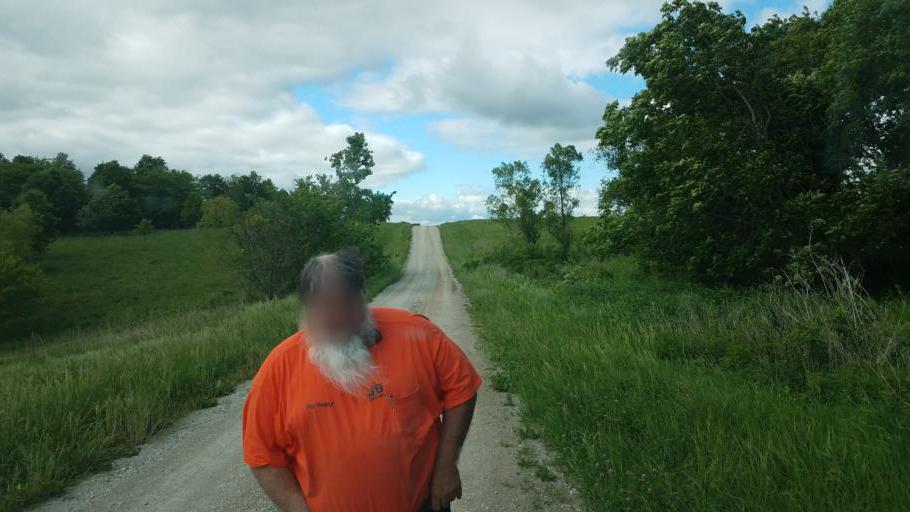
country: US
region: Missouri
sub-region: Grundy County
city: Trenton
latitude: 40.2513
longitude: -93.7077
